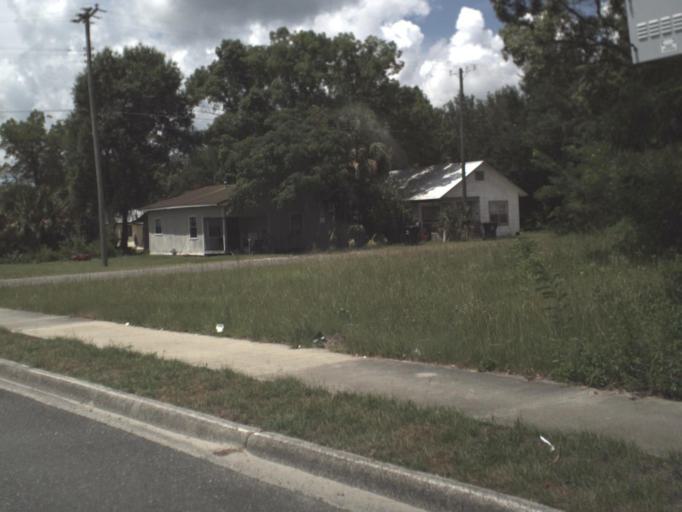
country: US
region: Florida
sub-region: Taylor County
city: Perry
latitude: 30.1139
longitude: -83.5893
